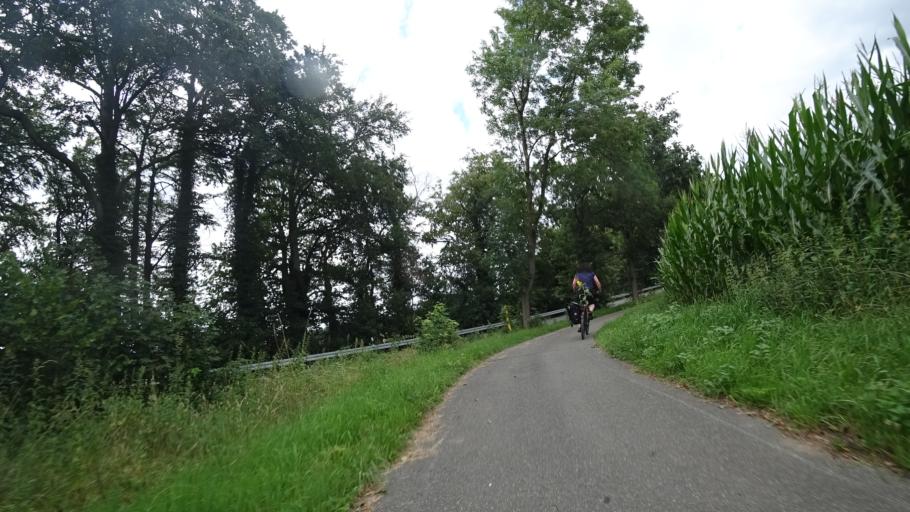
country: DE
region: Lower Saxony
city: Leese
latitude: 52.4707
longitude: 9.0884
